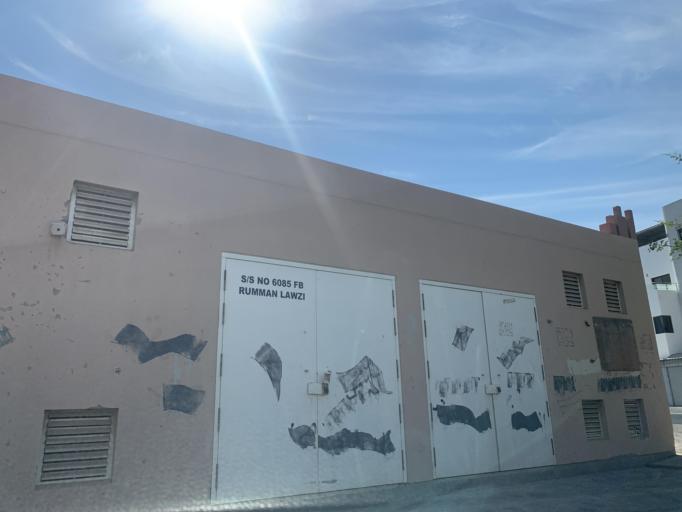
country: BH
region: Central Governorate
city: Madinat Hamad
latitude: 26.1176
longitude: 50.4852
